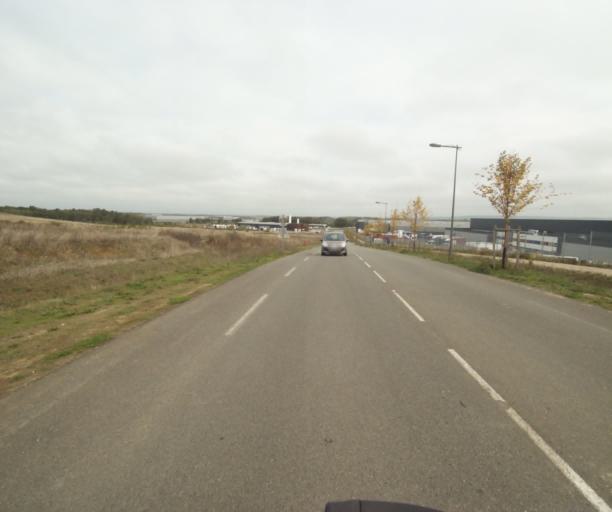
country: FR
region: Midi-Pyrenees
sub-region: Departement du Tarn-et-Garonne
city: Campsas
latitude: 43.9101
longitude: 1.3069
